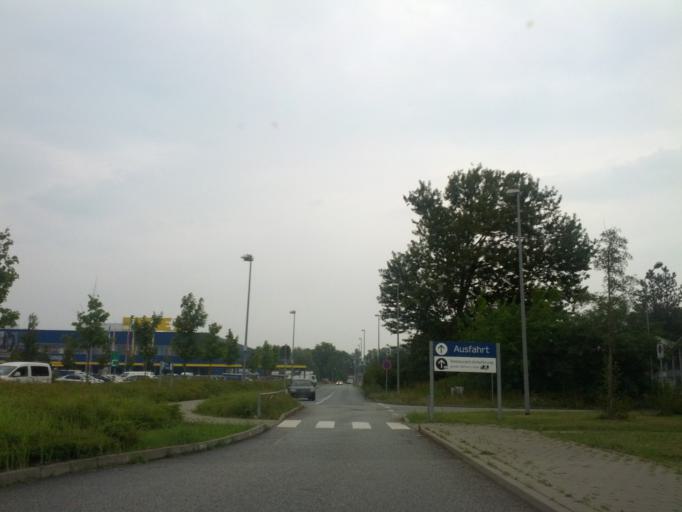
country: DE
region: Mecklenburg-Vorpommern
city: Lambrechtshagen
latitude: 54.1066
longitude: 12.0530
